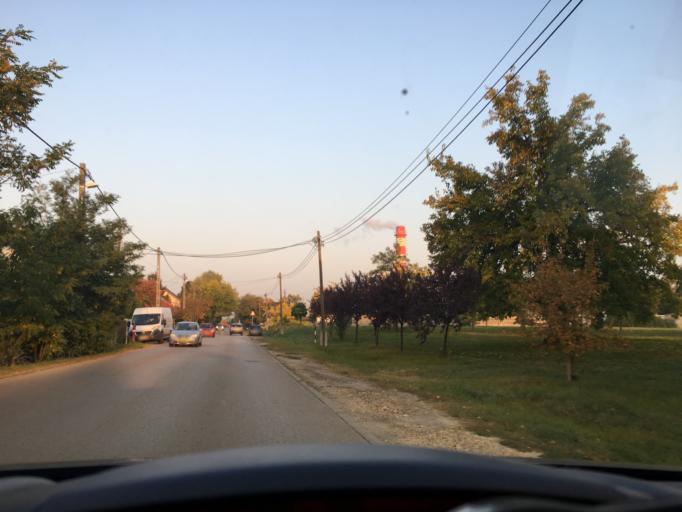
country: HU
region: Budapest
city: Budapest XVII. keruelet
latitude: 47.4762
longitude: 19.2483
